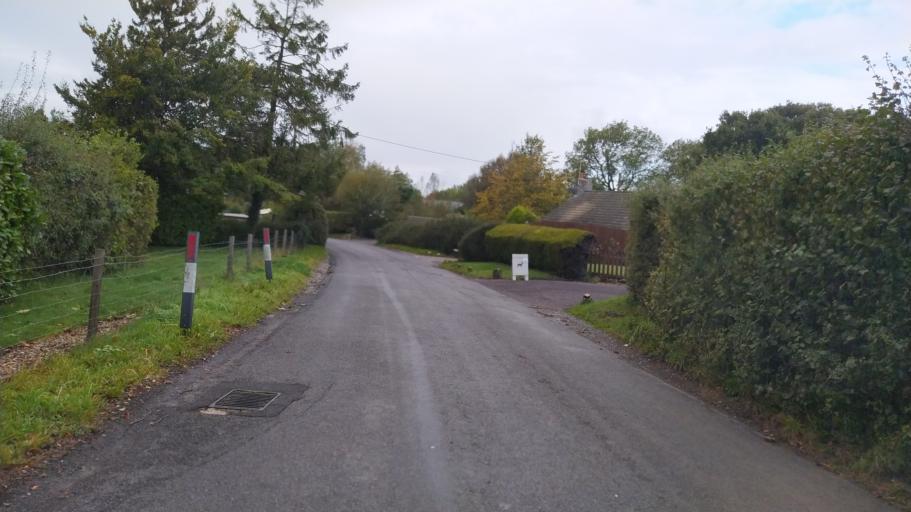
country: GB
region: England
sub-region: Dorset
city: Shaftesbury
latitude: 51.0416
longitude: -2.1925
